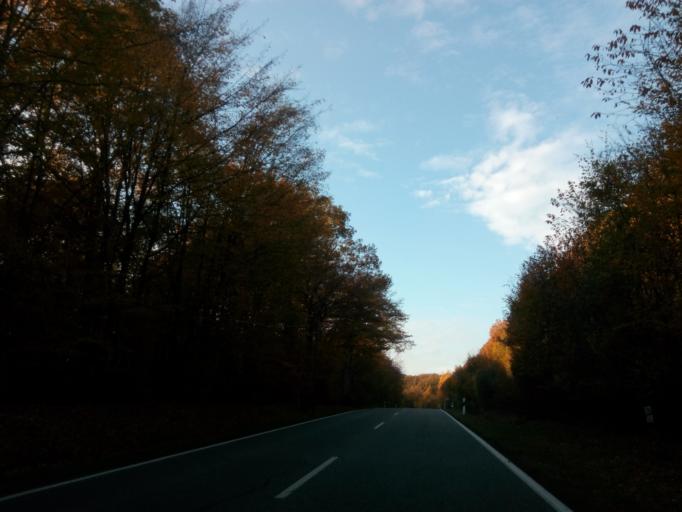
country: DE
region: Saarland
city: Riegelsberg
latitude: 49.2954
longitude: 6.9759
